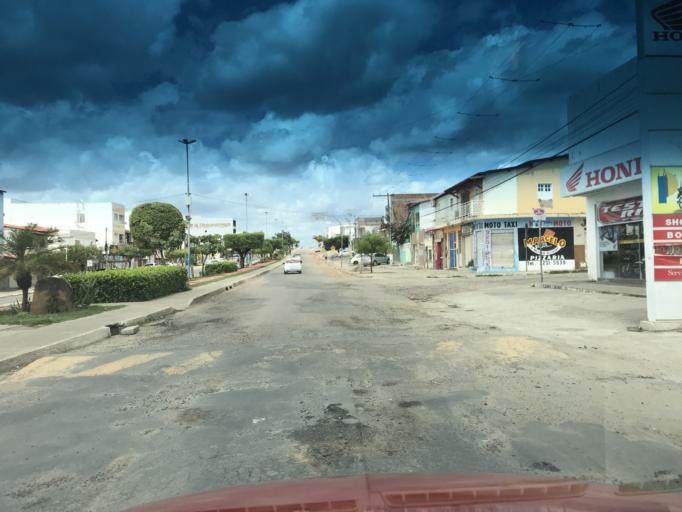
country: BR
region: Bahia
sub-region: Itaberaba
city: Itaberaba
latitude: -12.5229
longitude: -40.3063
